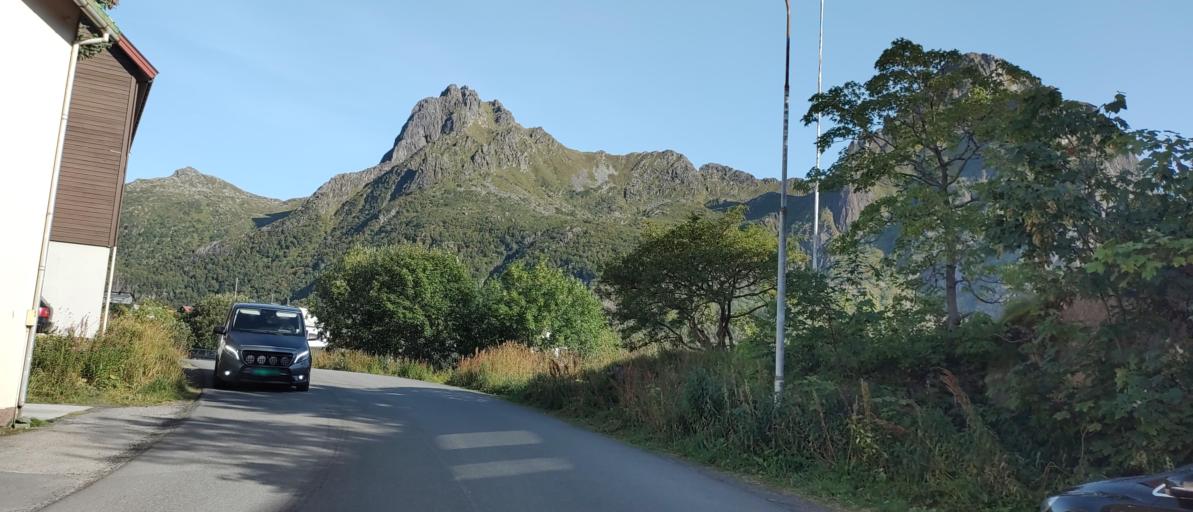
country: NO
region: Nordland
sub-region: Vagan
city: Svolvaer
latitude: 68.2374
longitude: 14.5714
